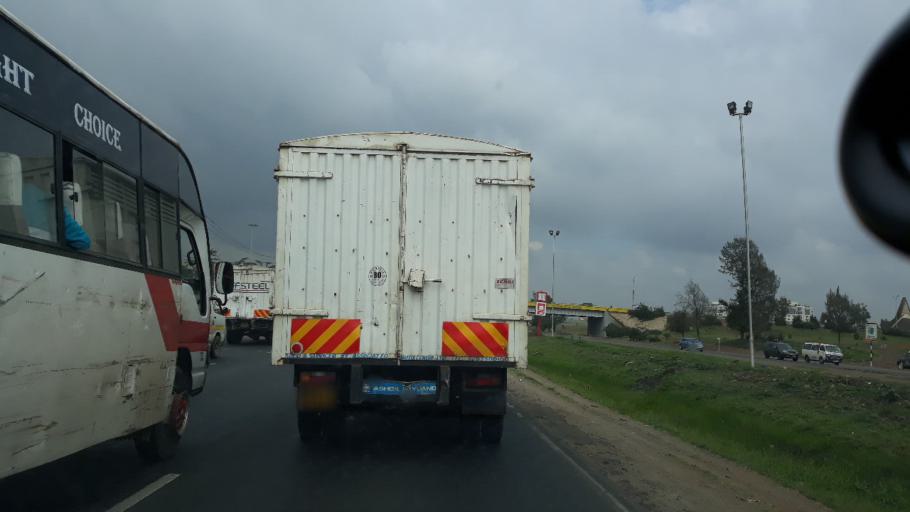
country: KE
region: Nairobi Area
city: Pumwani
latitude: -1.3331
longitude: 36.8896
